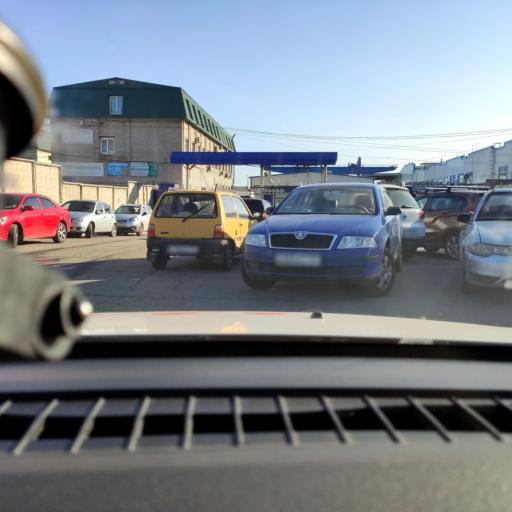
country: RU
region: Samara
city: Samara
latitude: 53.2011
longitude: 50.2621
